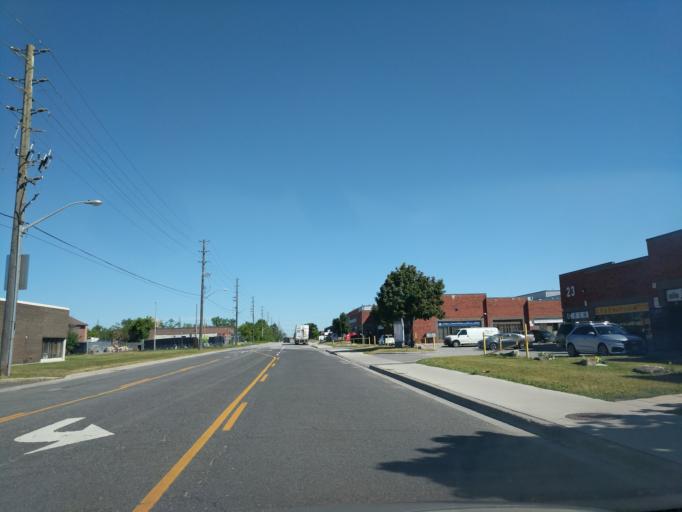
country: CA
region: Ontario
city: Scarborough
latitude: 43.8037
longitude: -79.2952
